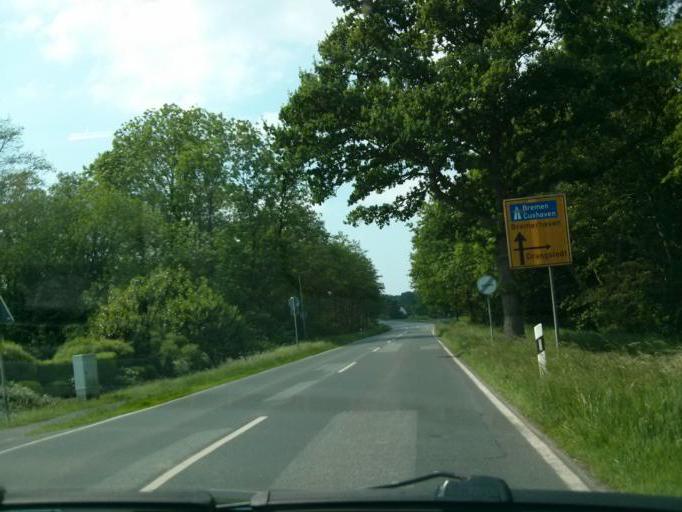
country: DE
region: Lower Saxony
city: Schiffdorf
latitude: 53.5231
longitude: 8.6671
